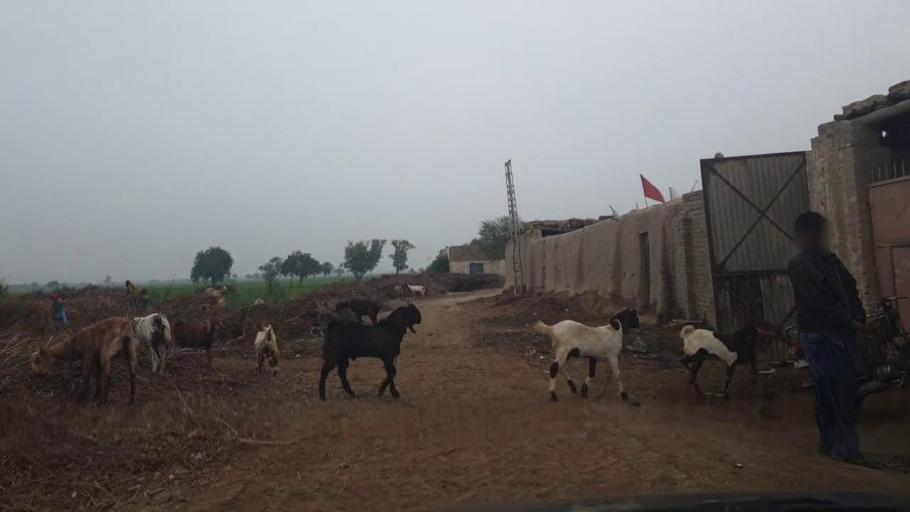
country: PK
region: Sindh
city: Tando Adam
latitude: 25.8094
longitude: 68.6792
